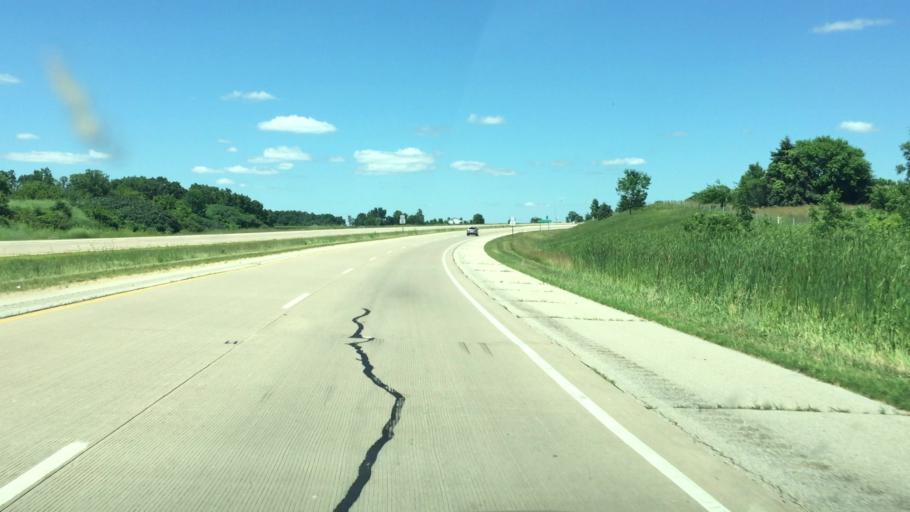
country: US
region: Wisconsin
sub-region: Grant County
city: Platteville
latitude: 42.6978
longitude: -90.5285
